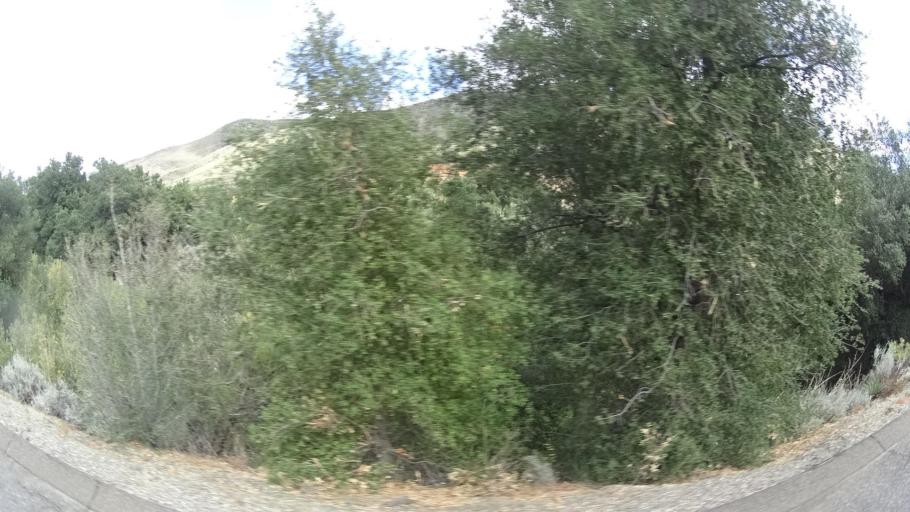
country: US
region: California
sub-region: San Diego County
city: Pine Valley
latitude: 32.7929
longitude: -116.4968
